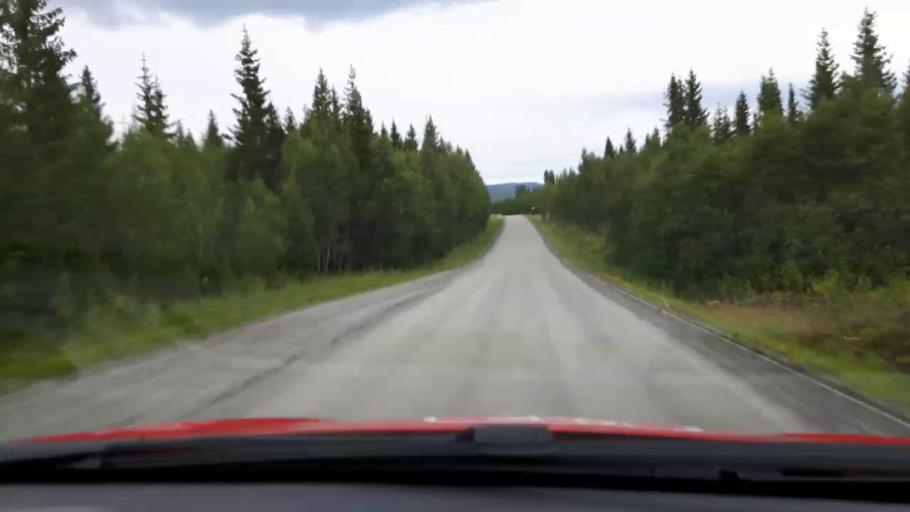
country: SE
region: Jaemtland
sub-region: Are Kommun
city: Are
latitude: 63.4446
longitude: 13.2226
